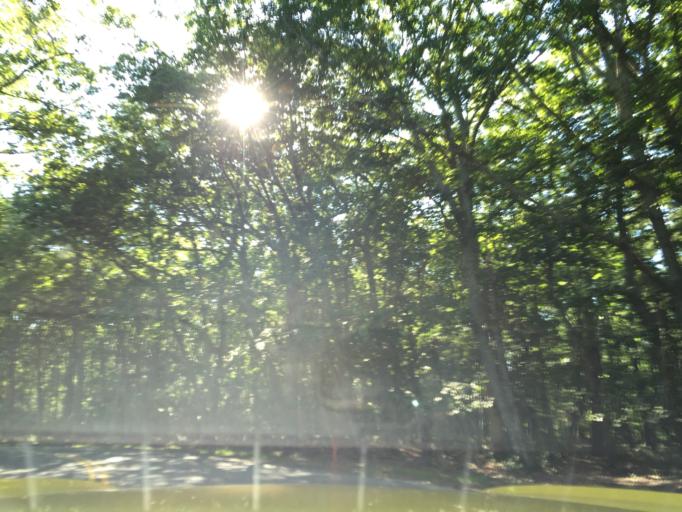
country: US
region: New York
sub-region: Suffolk County
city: Southold
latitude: 41.0443
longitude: -72.3922
